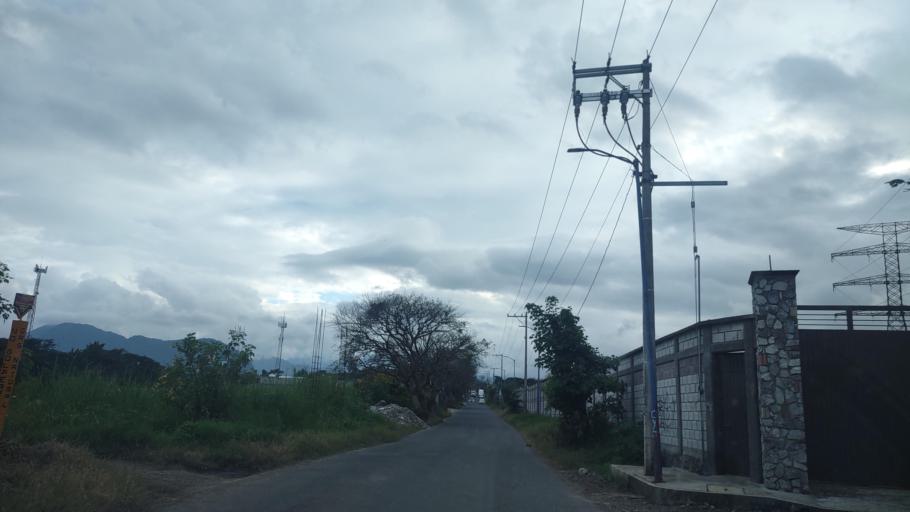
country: MX
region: Veracruz
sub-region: Ixtaczoquitlan
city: Buenavista
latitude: 18.8807
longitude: -97.0583
